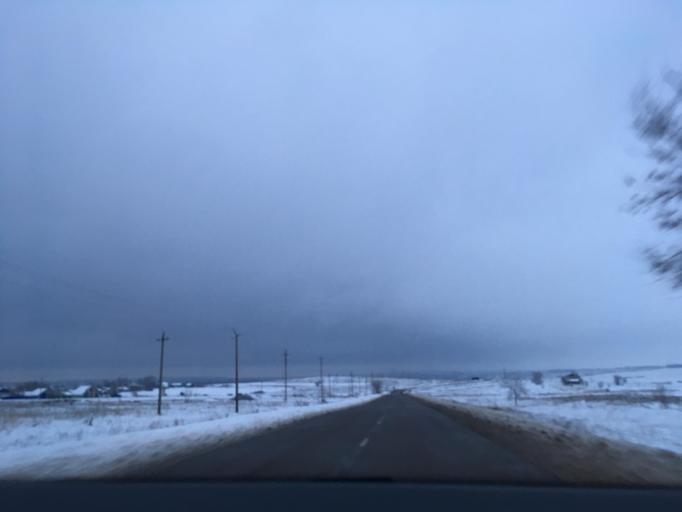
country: RU
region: Voronezj
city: Verkhniy Mamon
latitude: 50.0724
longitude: 40.3009
